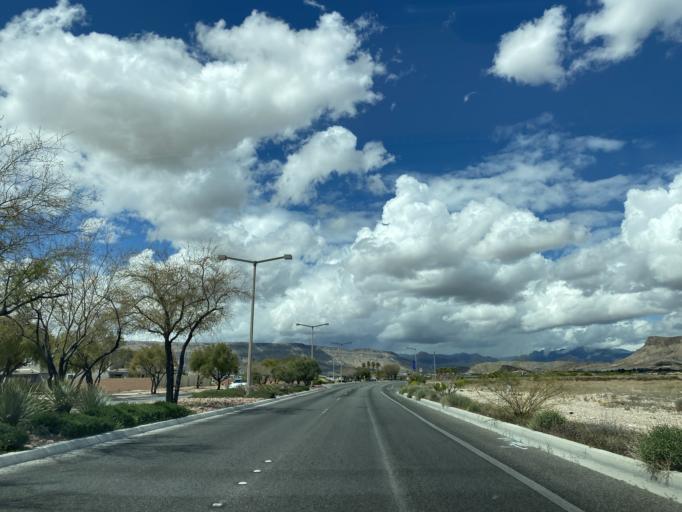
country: US
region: Nevada
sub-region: Clark County
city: Summerlin South
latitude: 36.1153
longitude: -115.3249
